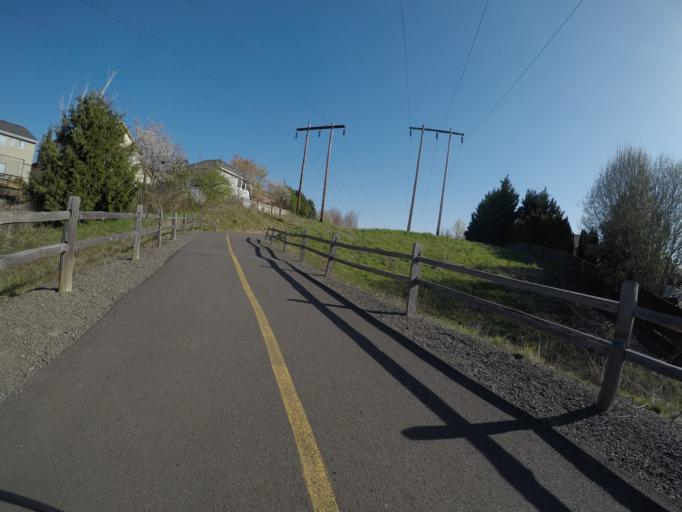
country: US
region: Oregon
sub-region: Washington County
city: Oak Hills
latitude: 45.5590
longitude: -122.8261
